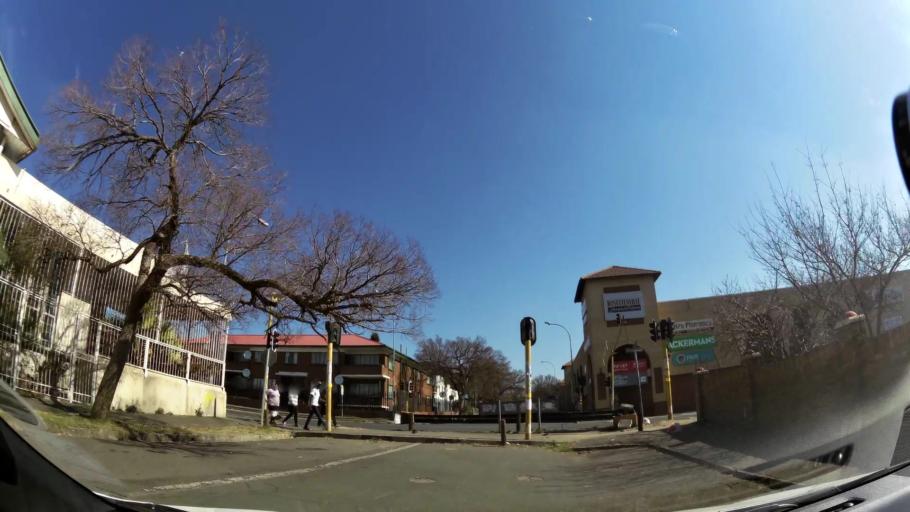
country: ZA
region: Gauteng
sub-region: City of Johannesburg Metropolitan Municipality
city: Johannesburg
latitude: -26.2449
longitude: 28.0557
